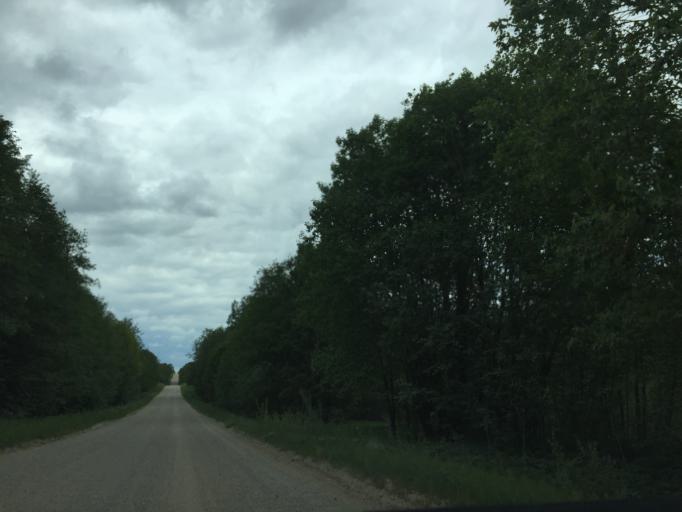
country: LV
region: Dagda
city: Dagda
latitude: 55.9972
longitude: 27.6099
